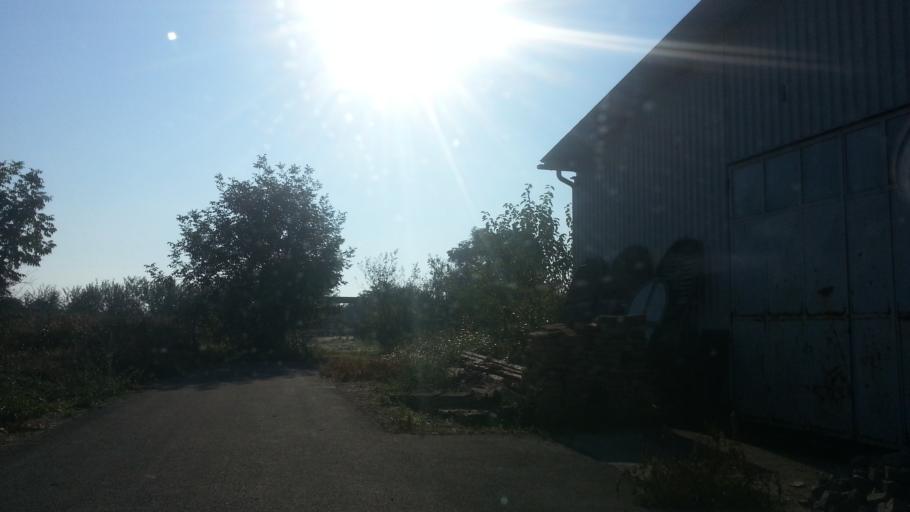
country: RS
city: Stari Banovci
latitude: 44.9861
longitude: 20.2693
